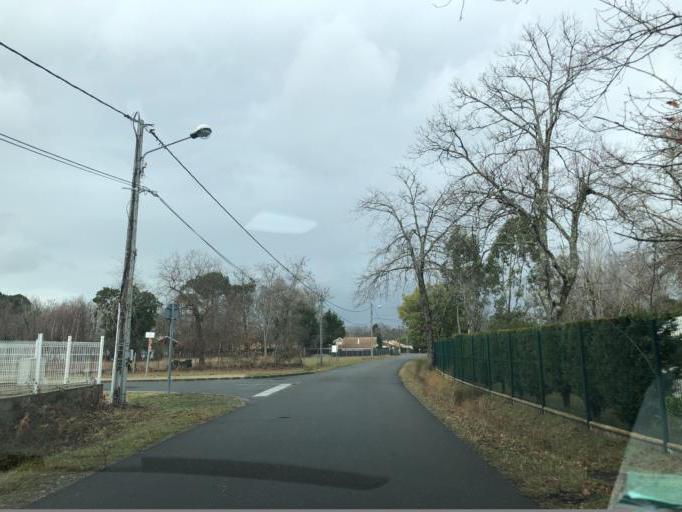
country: FR
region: Aquitaine
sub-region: Departement de la Gironde
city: Hourtin
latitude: 45.1806
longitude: -1.0755
